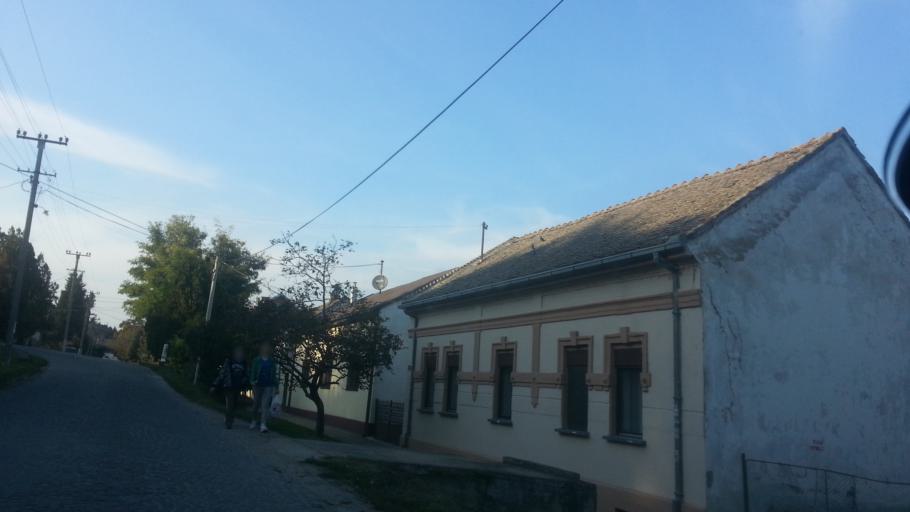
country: RS
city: Novi Slankamen
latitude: 45.1411
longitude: 20.2590
